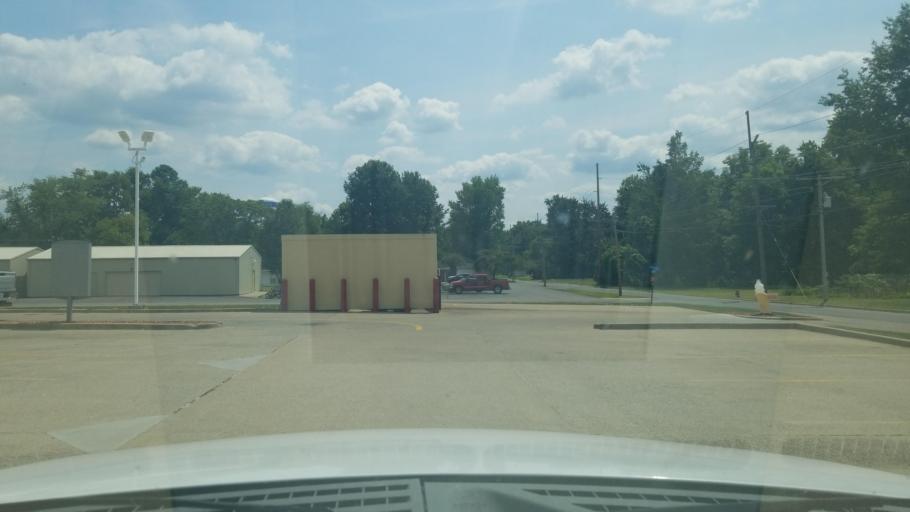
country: US
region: Illinois
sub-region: Williamson County
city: Marion
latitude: 37.7405
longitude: -88.9258
